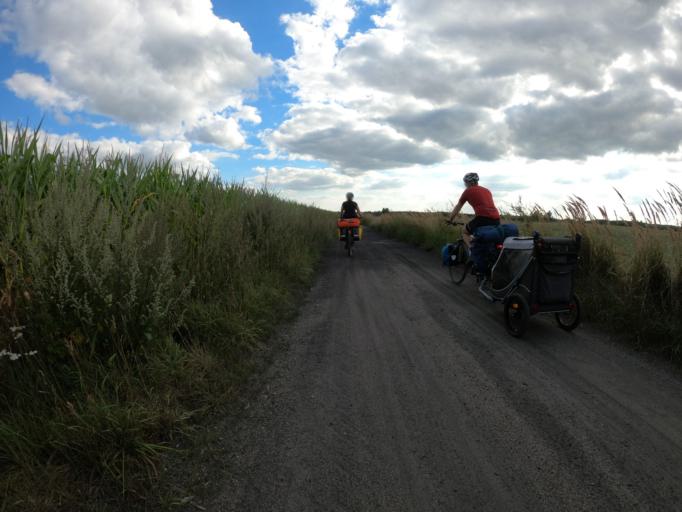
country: PL
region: West Pomeranian Voivodeship
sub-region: Powiat swidwinski
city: Swidwin
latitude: 53.7585
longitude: 15.6562
